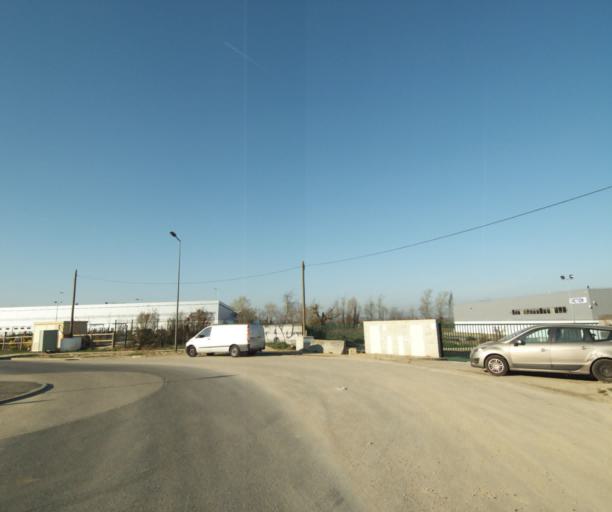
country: FR
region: Ile-de-France
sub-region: Departement du Val-d'Oise
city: Vaureal
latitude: 49.0566
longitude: 2.0327
